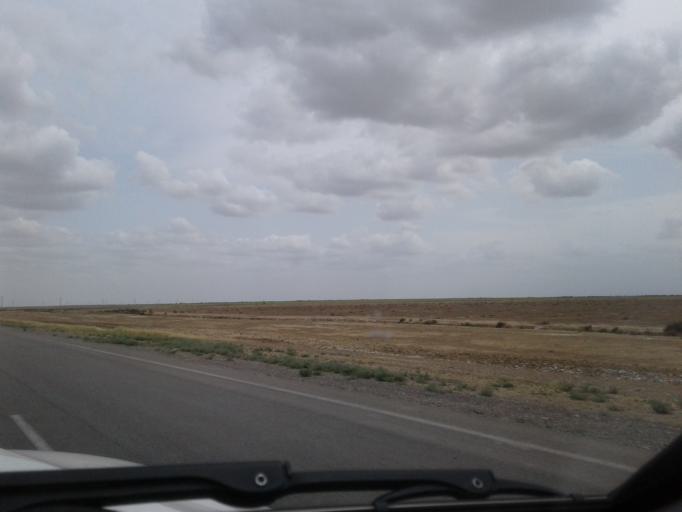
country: IR
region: Razavi Khorasan
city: Dargaz
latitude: 37.5929
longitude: 59.2661
